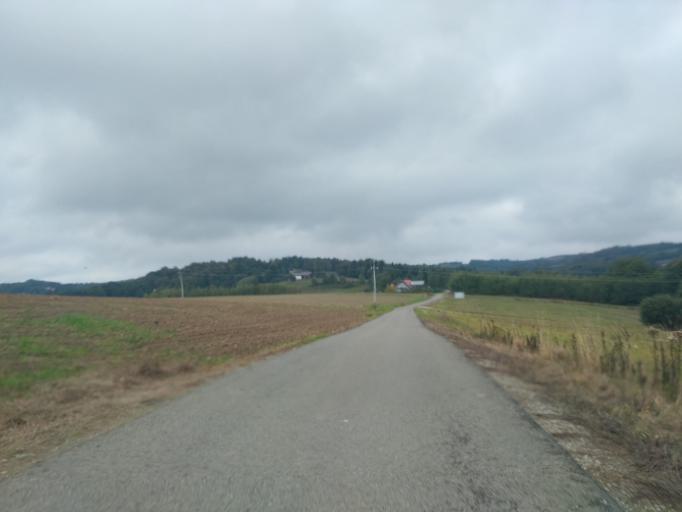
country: PL
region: Subcarpathian Voivodeship
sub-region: Powiat debicki
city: Brzostek
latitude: 49.9401
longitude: 21.4521
